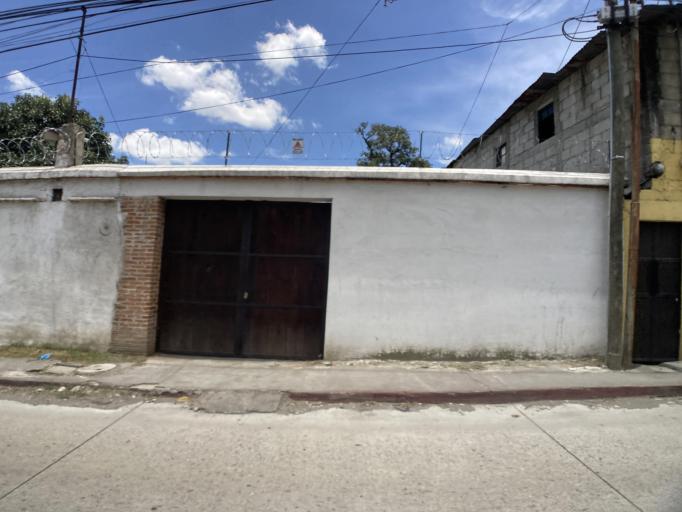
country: GT
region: Sacatepequez
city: Antigua Guatemala
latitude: 14.5441
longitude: -90.7294
